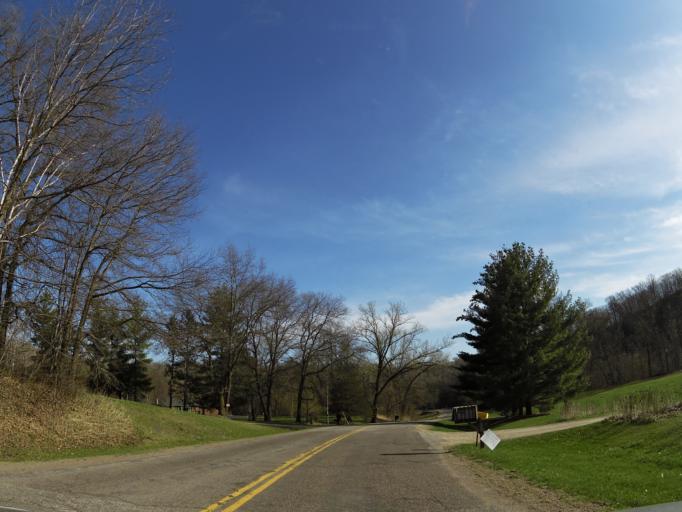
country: US
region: Wisconsin
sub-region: Pierce County
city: Ellsworth
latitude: 44.6938
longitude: -92.5787
